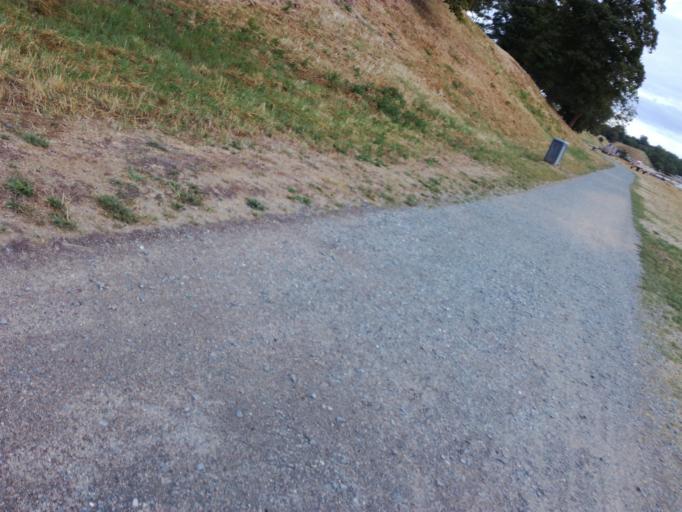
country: DK
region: South Denmark
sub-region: Fredericia Kommune
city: Fredericia
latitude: 55.5616
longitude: 9.7685
